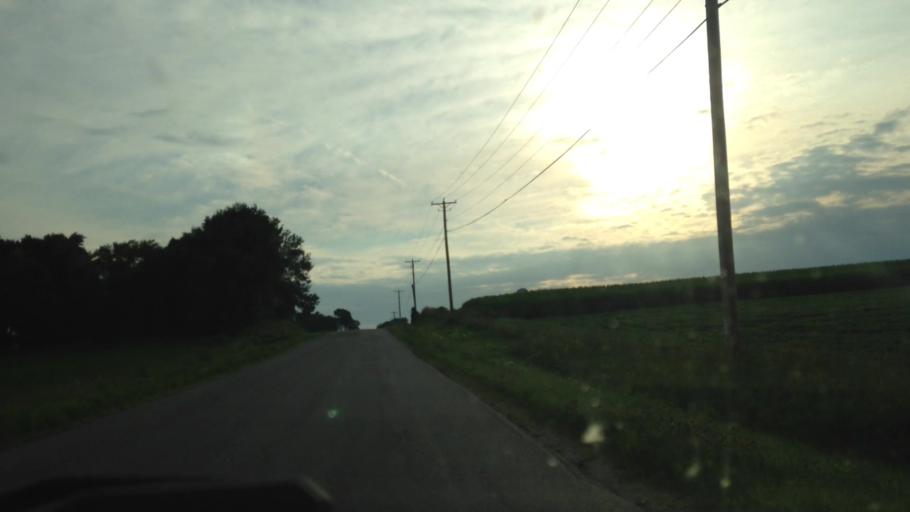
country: US
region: Wisconsin
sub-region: Dodge County
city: Mayville
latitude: 43.4932
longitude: -88.5039
